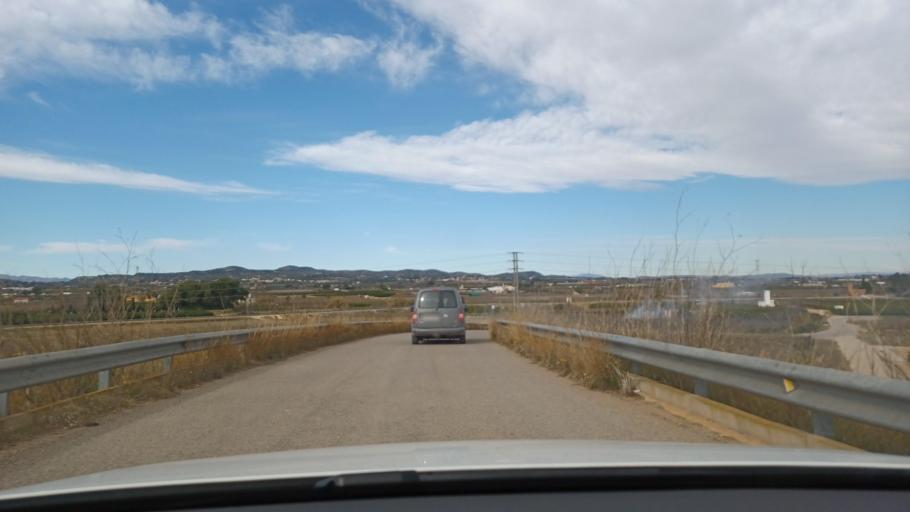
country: ES
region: Valencia
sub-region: Provincia de Valencia
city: Benifaio
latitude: 39.2918
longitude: -0.4375
